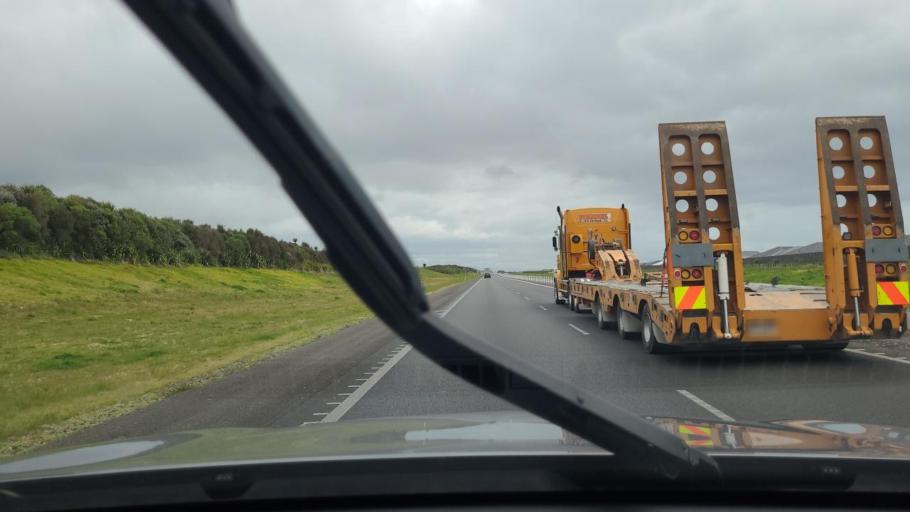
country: NZ
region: Bay of Plenty
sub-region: Western Bay of Plenty District
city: Maketu
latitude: -37.7317
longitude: 176.3412
